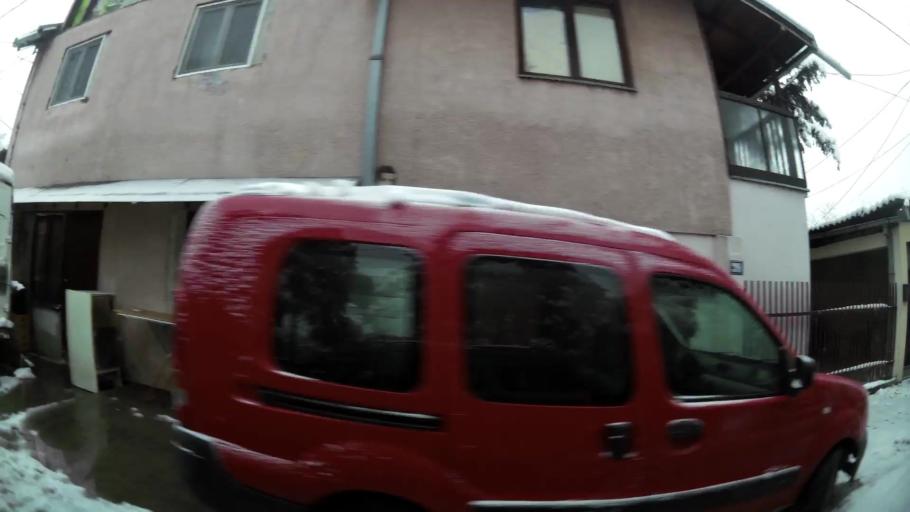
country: RS
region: Central Serbia
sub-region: Belgrade
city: Novi Beograd
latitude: 44.8092
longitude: 20.4417
